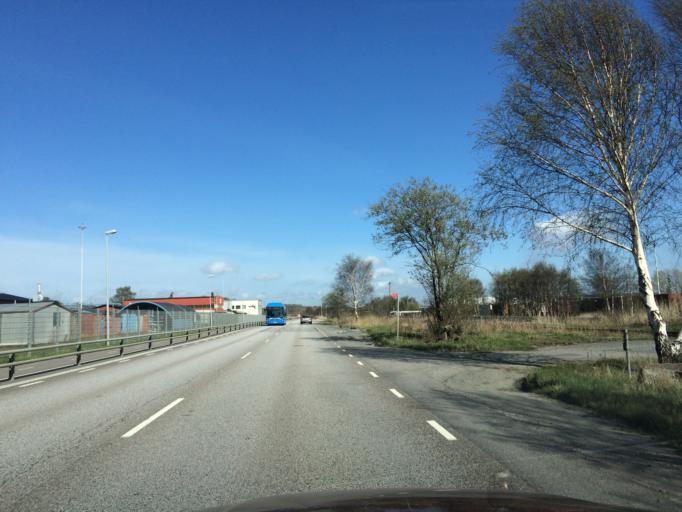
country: SE
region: Vaestra Goetaland
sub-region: Goteborg
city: Majorna
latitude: 57.6977
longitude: 11.8463
